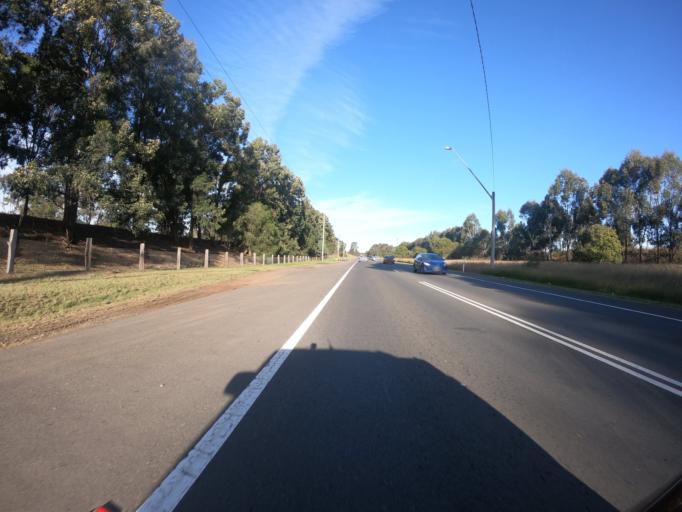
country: AU
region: New South Wales
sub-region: Hawkesbury
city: South Windsor
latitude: -33.6706
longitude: 150.8058
